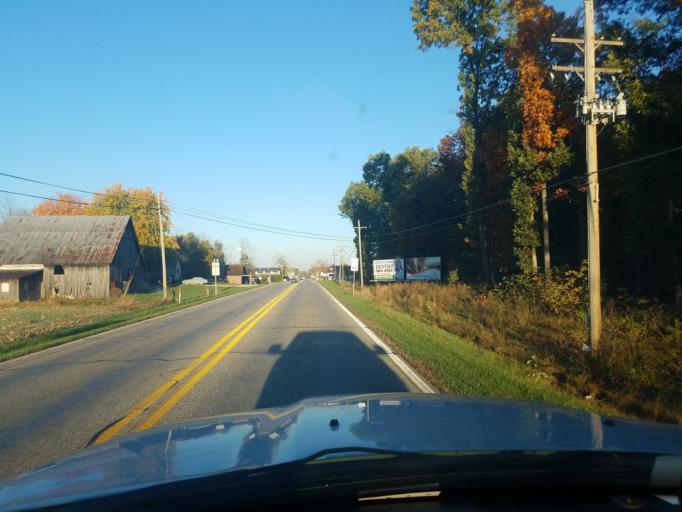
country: US
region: Indiana
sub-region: Washington County
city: New Pekin
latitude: 38.4063
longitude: -86.1046
